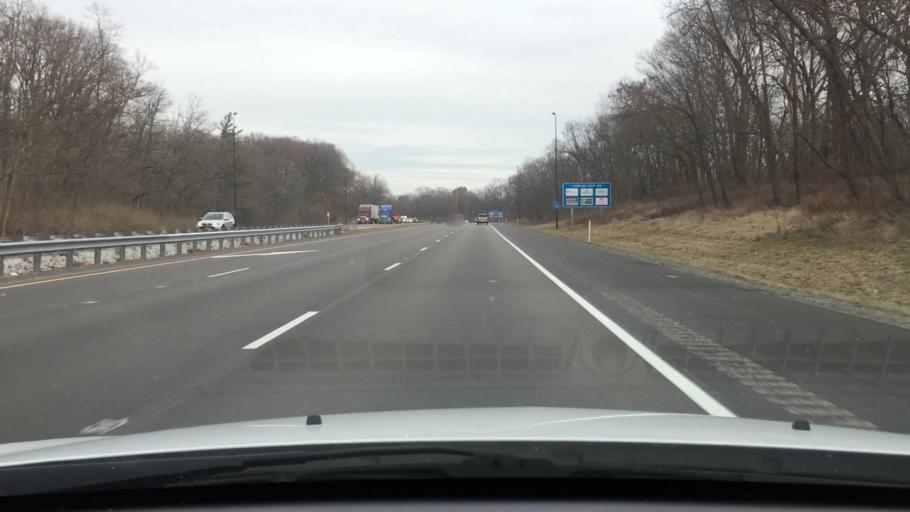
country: US
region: Illinois
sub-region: Sangamon County
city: Southern View
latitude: 39.7452
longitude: -89.6279
